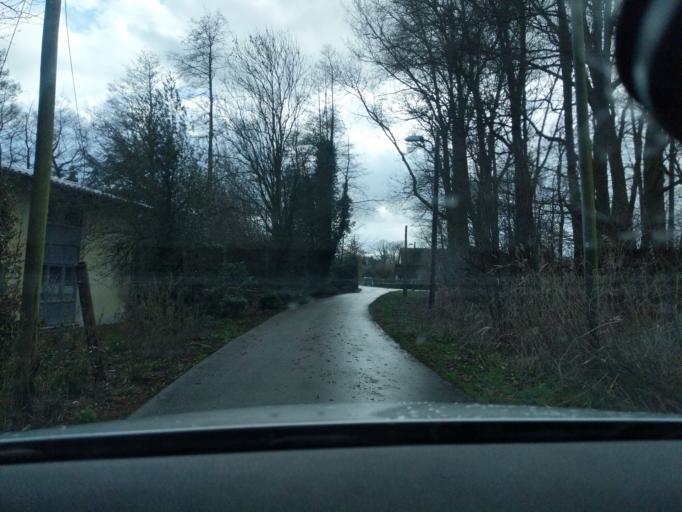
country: DE
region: Lower Saxony
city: Kranenburg
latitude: 53.6117
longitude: 9.2022
